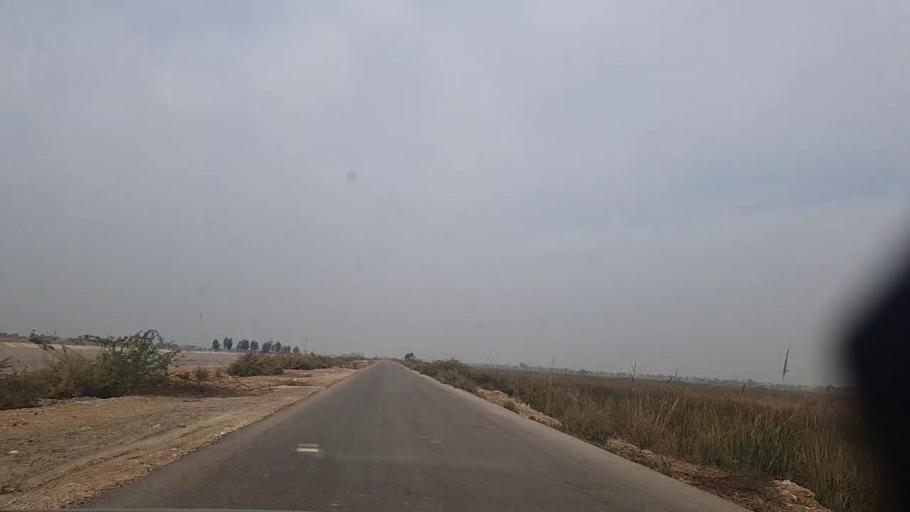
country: PK
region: Sindh
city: Sakrand
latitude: 26.2664
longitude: 68.2385
